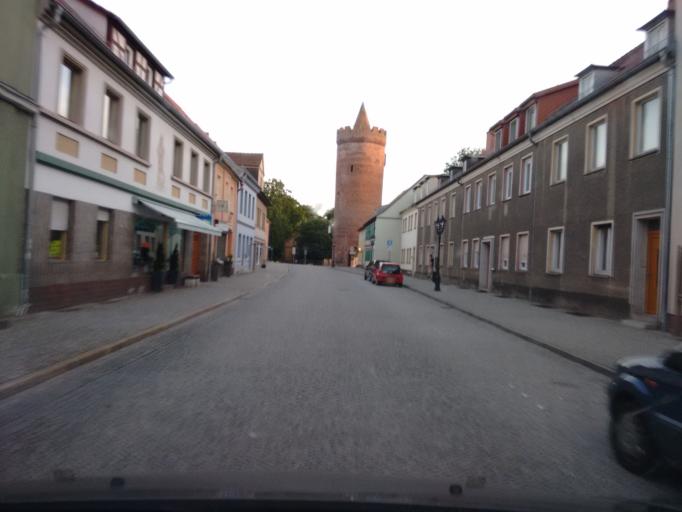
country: DE
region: Brandenburg
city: Beeskow
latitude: 52.1712
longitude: 14.2461
